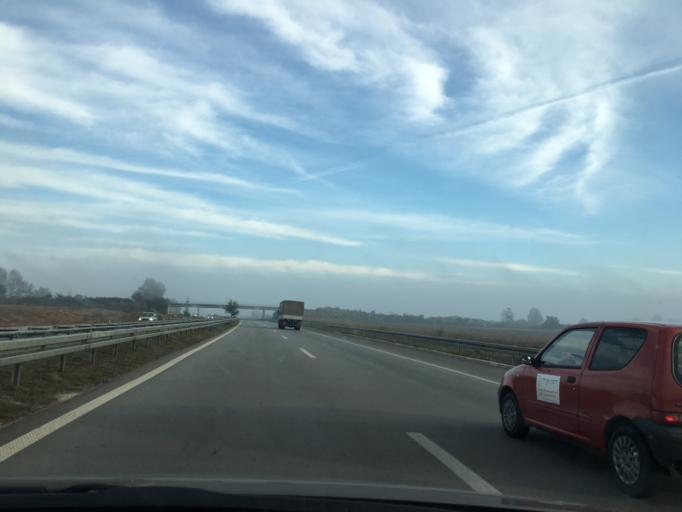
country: RS
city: Novi Banovci
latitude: 44.9136
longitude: 20.3054
